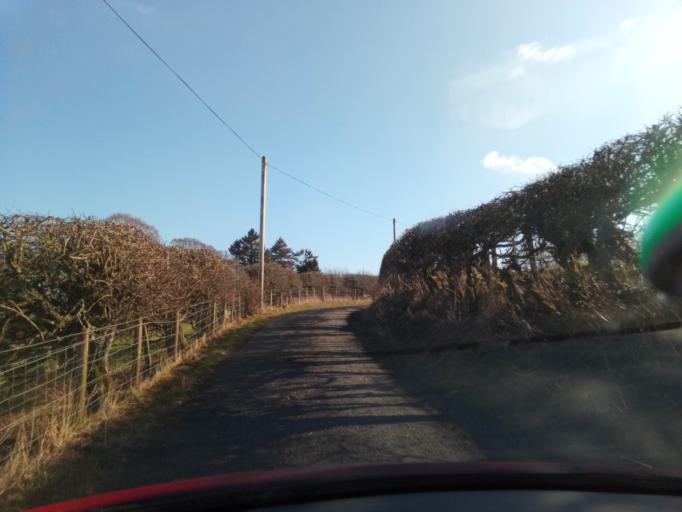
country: GB
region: Scotland
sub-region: The Scottish Borders
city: Selkirk
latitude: 55.4973
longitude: -2.7892
